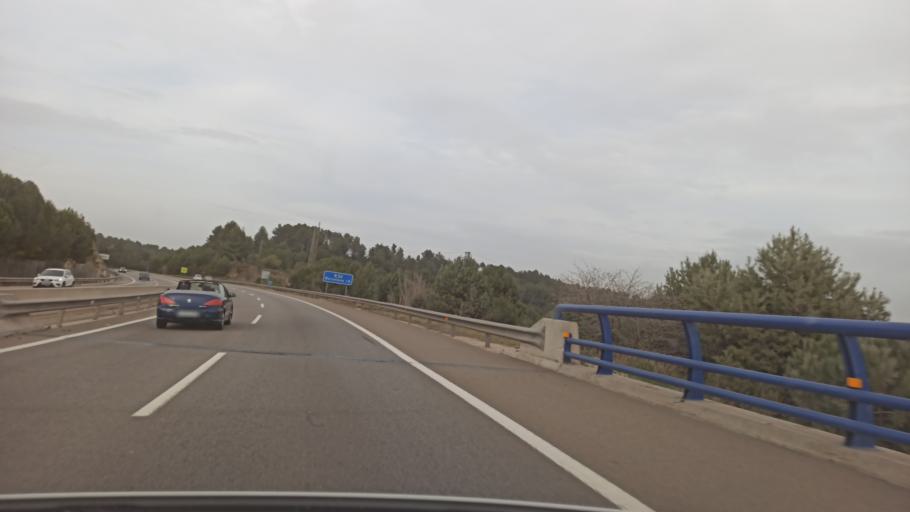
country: ES
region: Catalonia
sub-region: Provincia de Barcelona
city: Palleja
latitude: 41.4075
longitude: 1.9893
